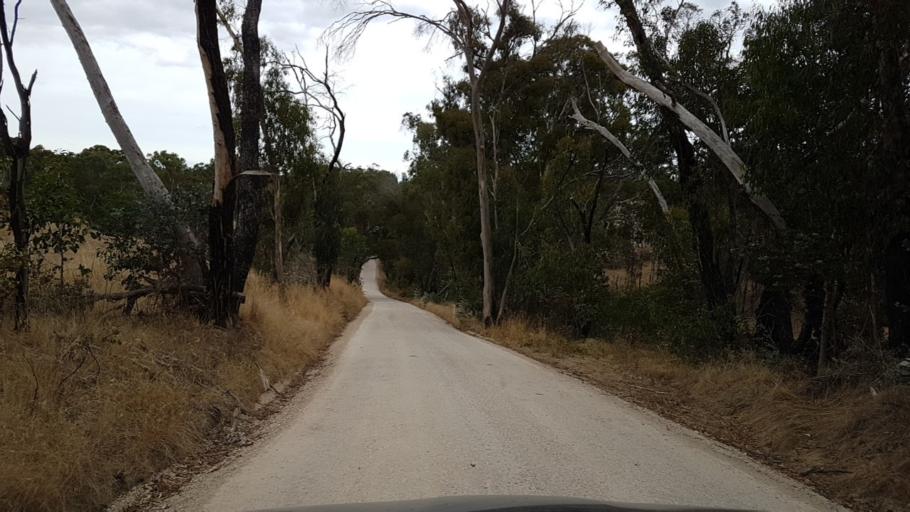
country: AU
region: South Australia
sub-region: Adelaide Hills
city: Gumeracha
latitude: -34.7990
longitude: 138.8340
